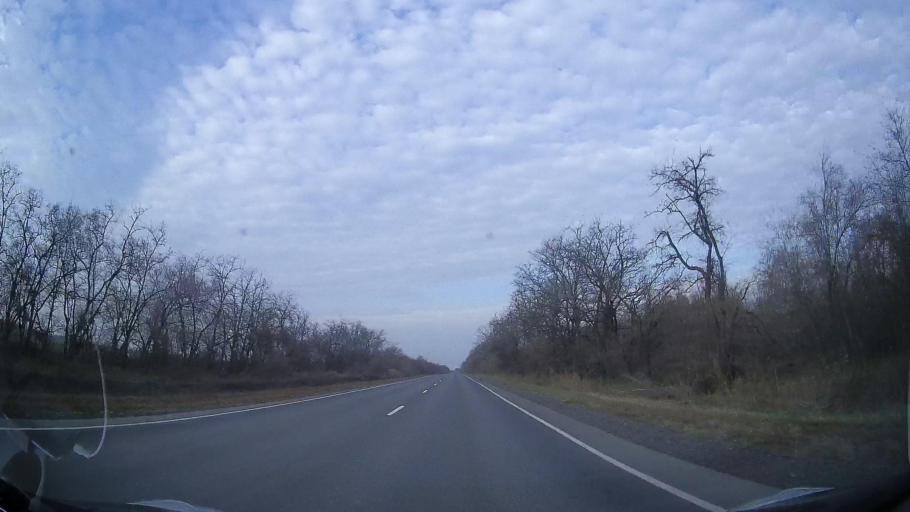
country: RU
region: Rostov
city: Bagayevskaya
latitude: 47.1251
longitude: 40.2767
